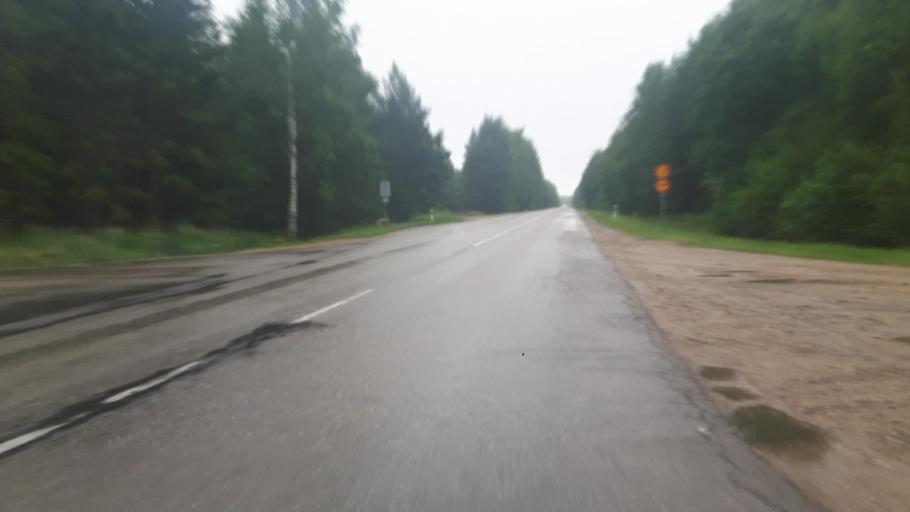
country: LV
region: Rucavas
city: Rucava
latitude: 56.1220
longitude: 21.1455
